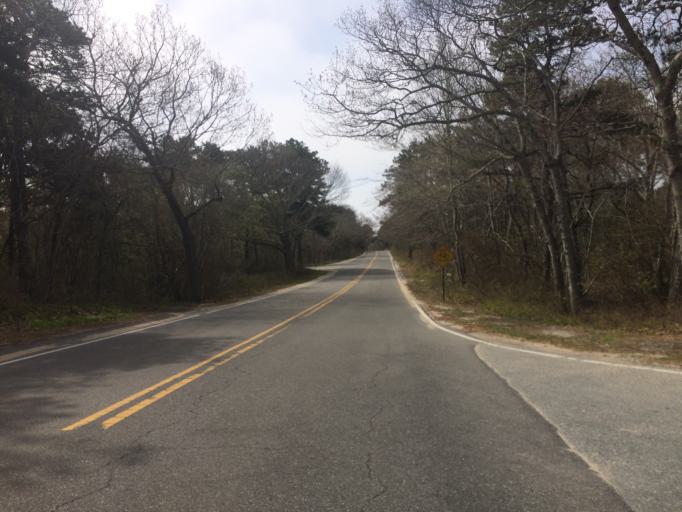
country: US
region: Massachusetts
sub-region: Barnstable County
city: Provincetown
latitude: 42.0657
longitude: -70.1929
